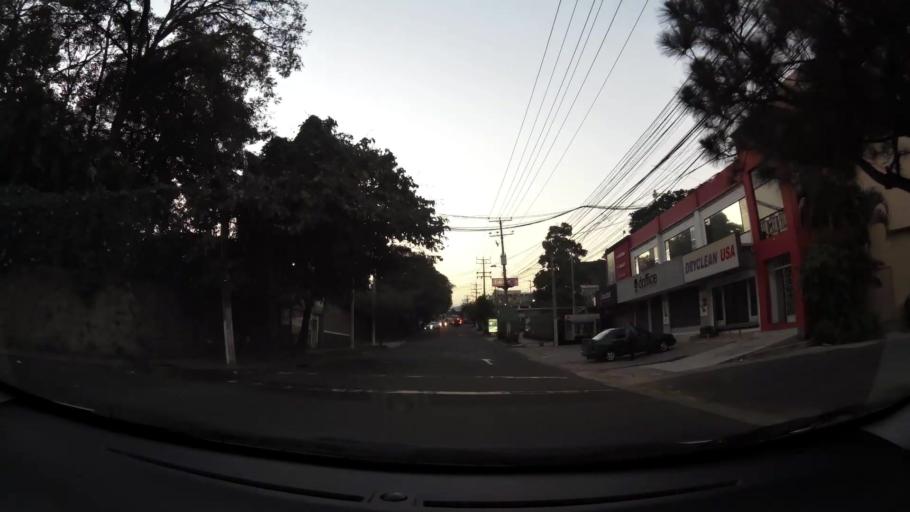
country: SV
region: La Libertad
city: Antiguo Cuscatlan
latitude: 13.6973
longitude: -89.2344
